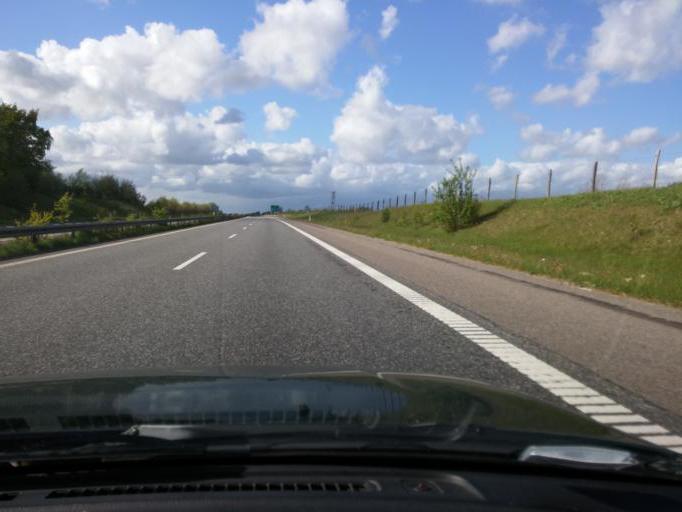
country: DK
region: South Denmark
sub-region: Faaborg-Midtfyn Kommune
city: Ringe
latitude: 55.2624
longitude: 10.4694
